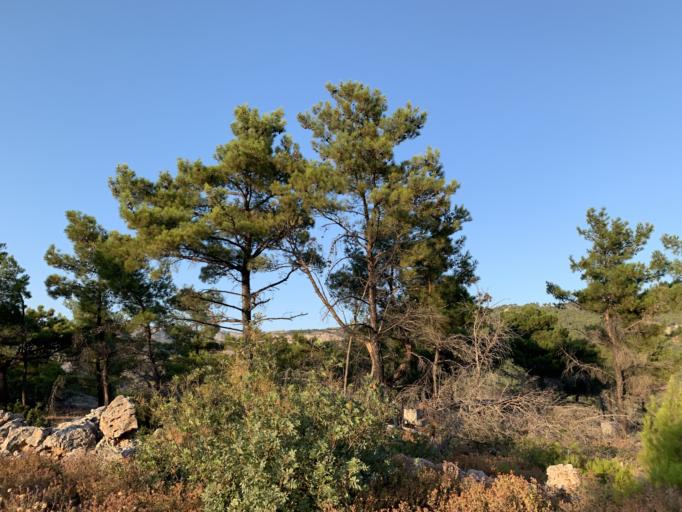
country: GR
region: North Aegean
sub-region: Chios
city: Chios
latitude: 38.3797
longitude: 26.0191
